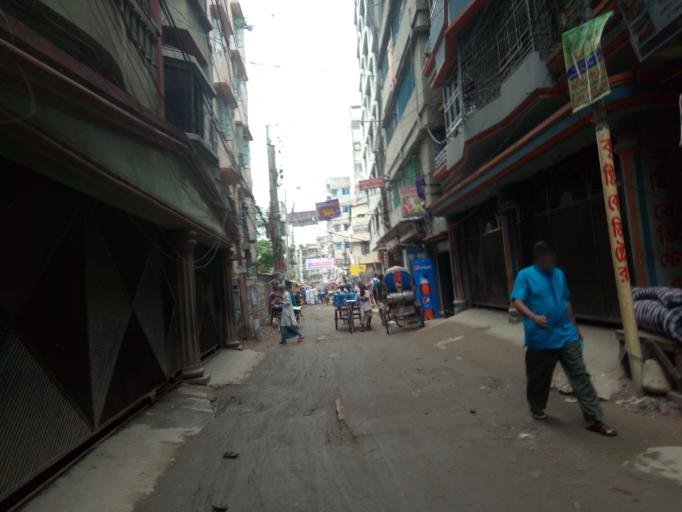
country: BD
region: Dhaka
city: Paltan
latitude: 23.7323
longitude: 90.4316
